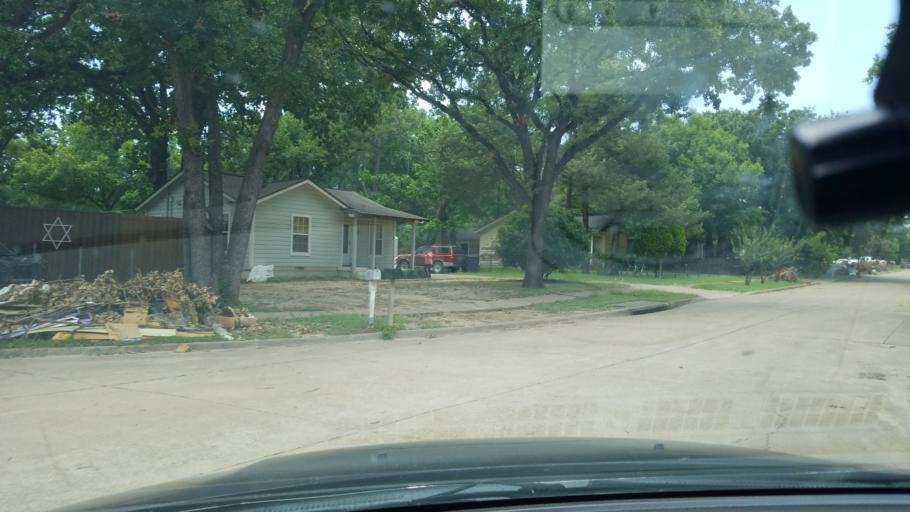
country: US
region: Texas
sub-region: Dallas County
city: Balch Springs
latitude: 32.7165
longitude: -96.6606
